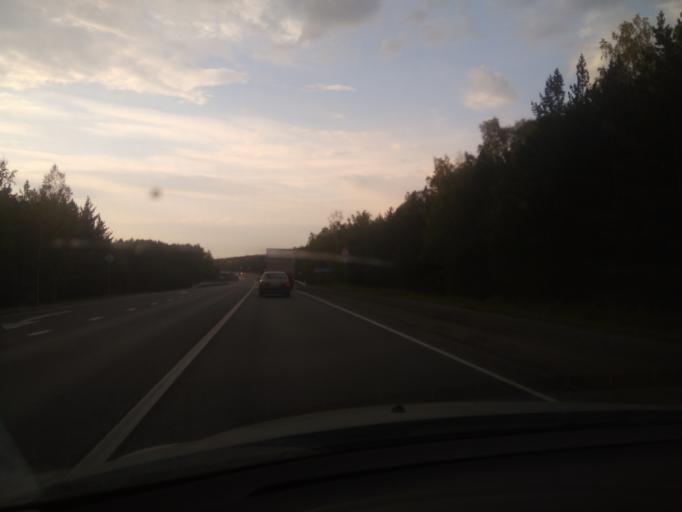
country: RU
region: Sverdlovsk
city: Verkhneye Dubrovo
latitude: 56.7178
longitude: 61.0545
